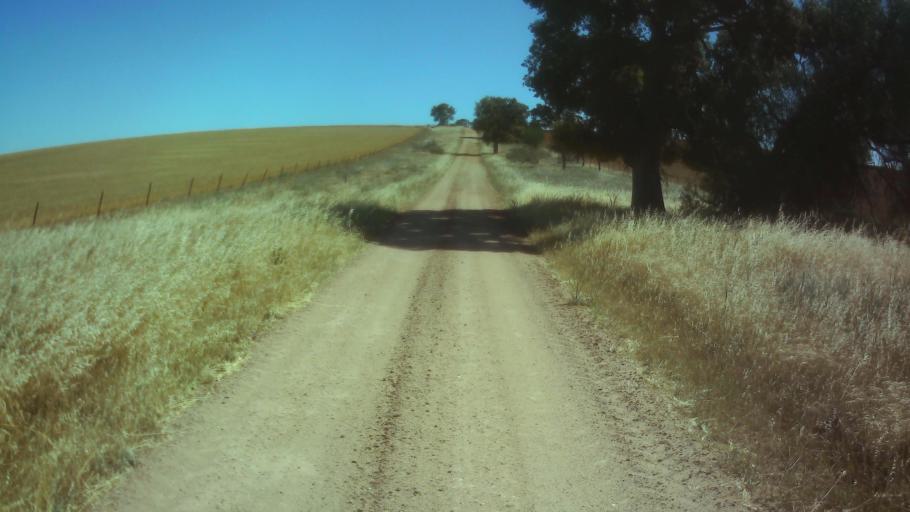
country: AU
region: New South Wales
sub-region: Weddin
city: Grenfell
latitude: -33.9722
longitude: 148.3434
